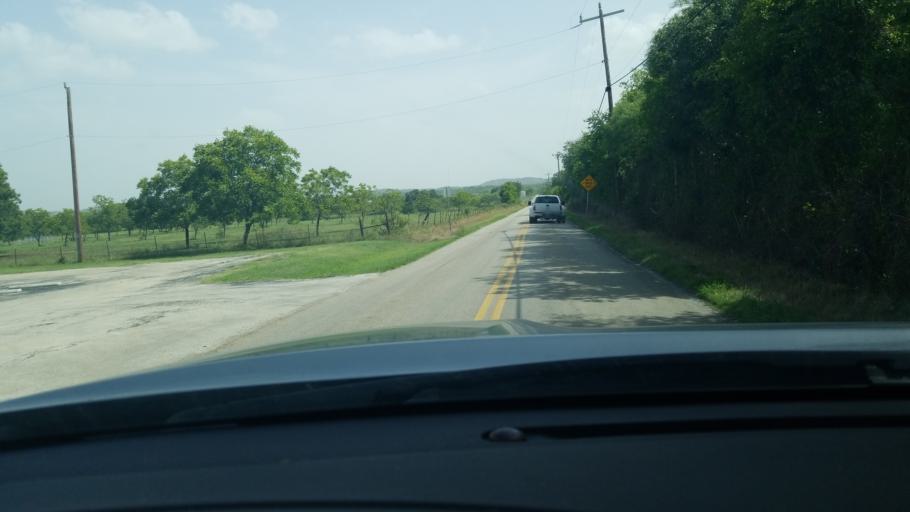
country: US
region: Texas
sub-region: Comal County
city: Bulverde
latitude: 29.7431
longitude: -98.4536
